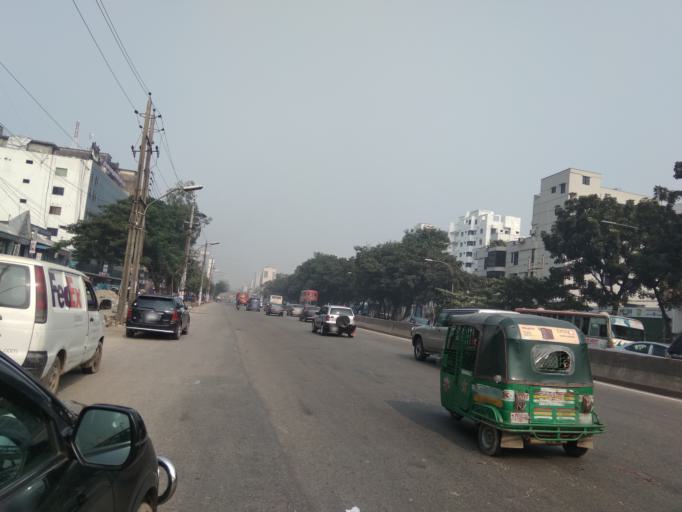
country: BD
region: Dhaka
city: Tungi
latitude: 23.8648
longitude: 90.4000
